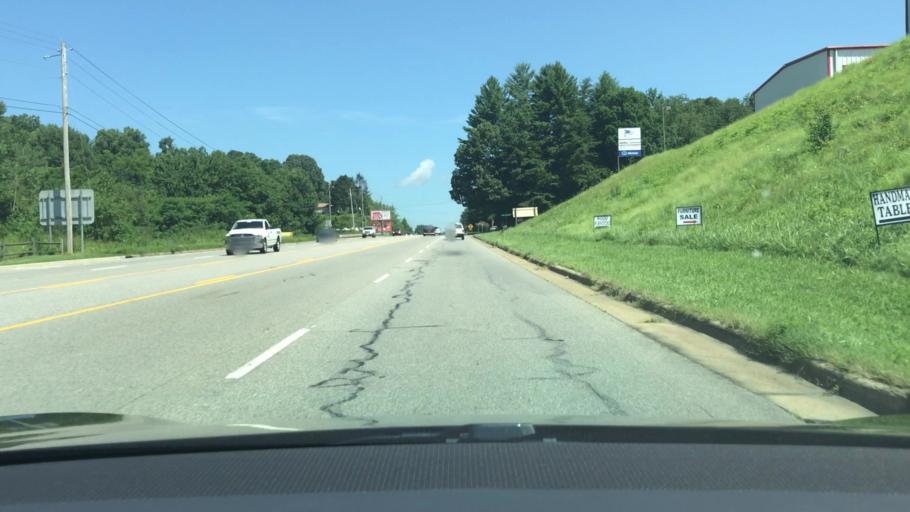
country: US
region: North Carolina
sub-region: Macon County
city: Franklin
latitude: 35.1139
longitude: -83.3898
